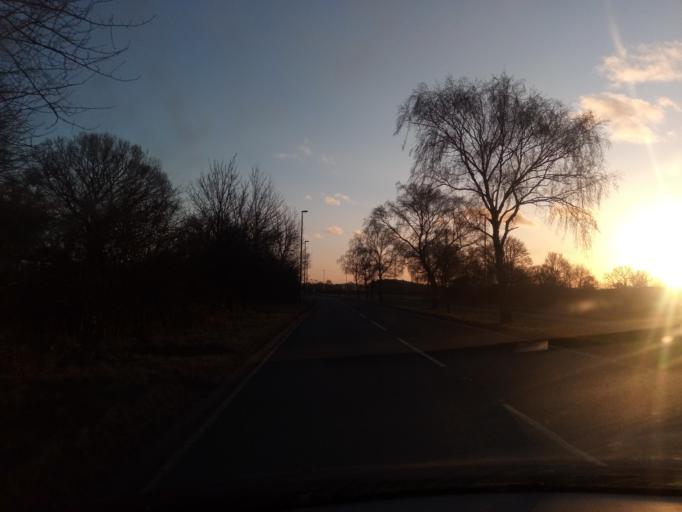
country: GB
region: England
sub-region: Nottinghamshire
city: Farnsfield
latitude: 53.0690
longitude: -1.0703
